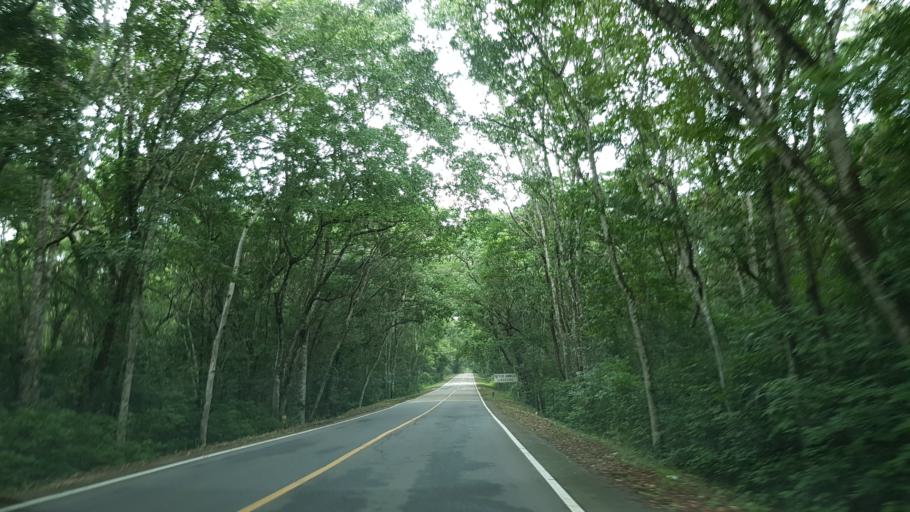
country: GT
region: Peten
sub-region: Municipio de San Jose
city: San Jose
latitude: 17.1823
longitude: -89.6340
